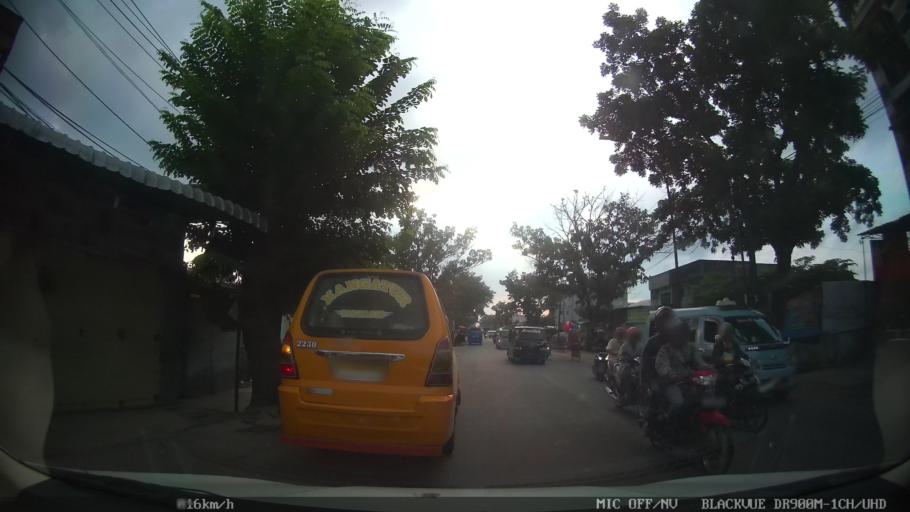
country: ID
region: North Sumatra
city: Medan
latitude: 3.5969
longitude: 98.7400
